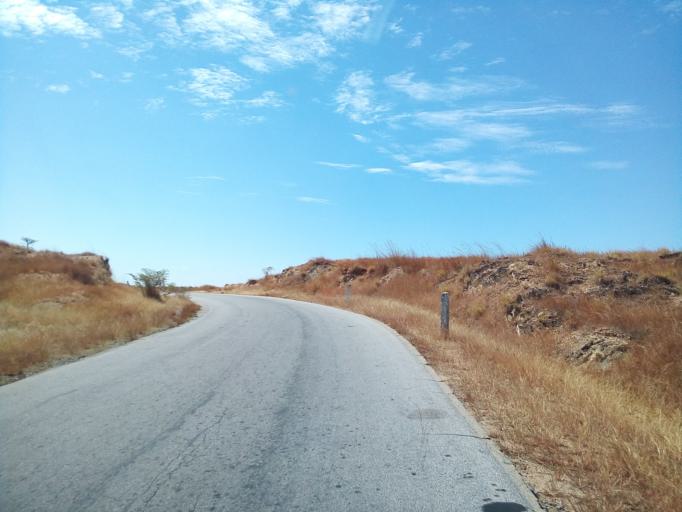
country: MG
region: Betsiboka
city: Maevatanana
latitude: -16.9495
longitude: 46.8544
